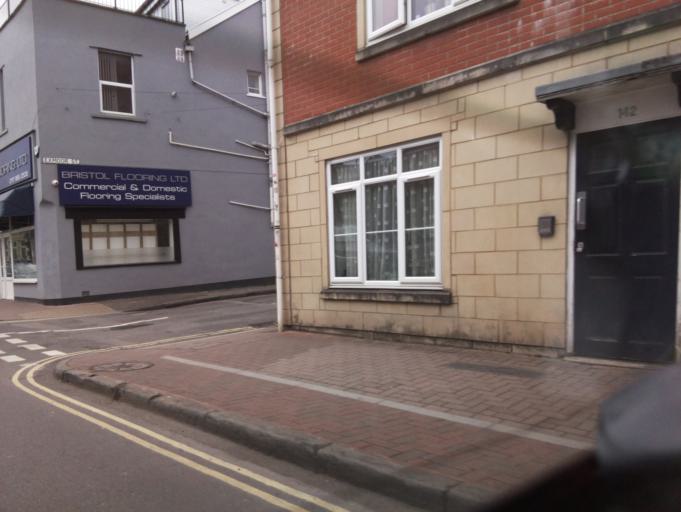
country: GB
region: England
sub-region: Bristol
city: Bristol
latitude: 51.4402
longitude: -2.6075
